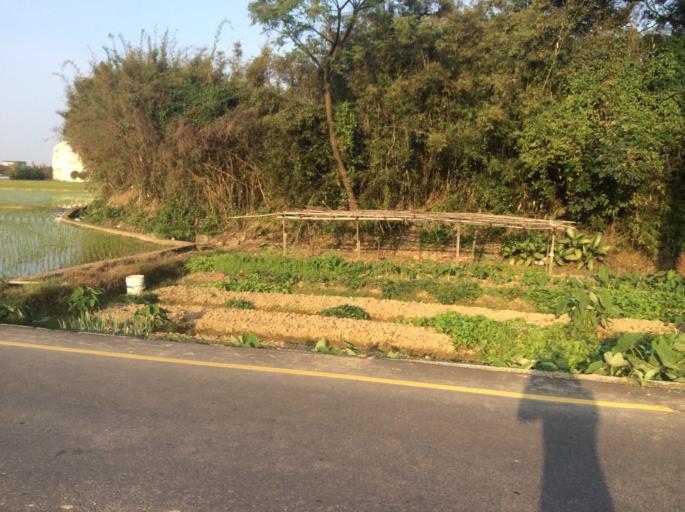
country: TW
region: Taiwan
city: Taoyuan City
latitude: 24.9762
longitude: 121.2061
